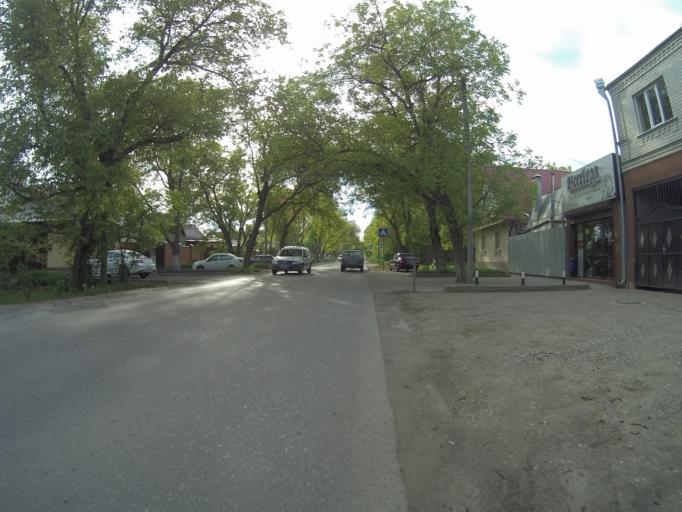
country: RU
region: Stavropol'skiy
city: Svobody
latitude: 44.0409
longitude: 43.0087
